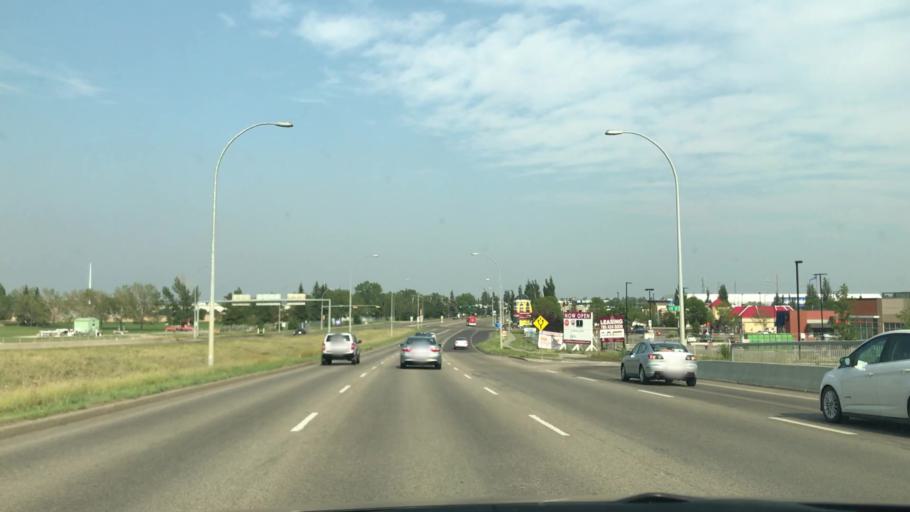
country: CA
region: Alberta
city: Edmonton
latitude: 53.4537
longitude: -113.4901
